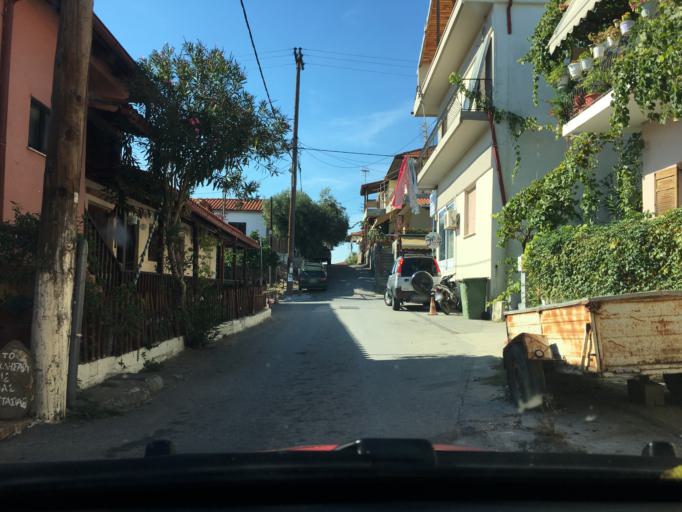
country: GR
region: Central Macedonia
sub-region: Nomos Chalkidikis
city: Ouranoupolis
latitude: 40.3267
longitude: 23.9811
